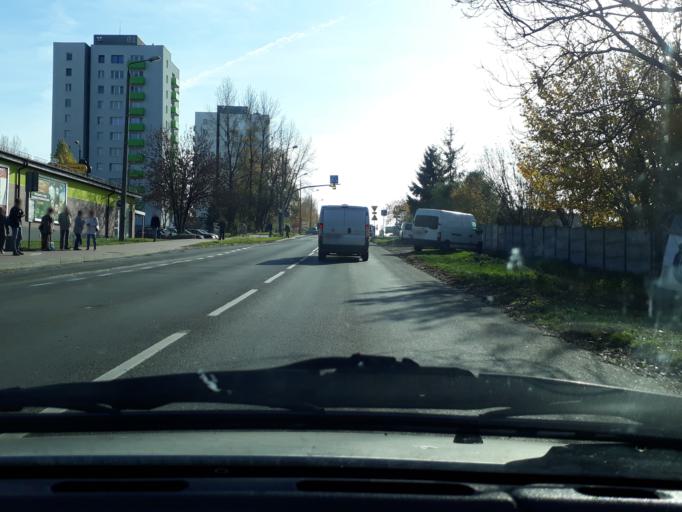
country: PL
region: Silesian Voivodeship
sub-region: Powiat tarnogorski
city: Tarnowskie Gory
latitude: 50.4337
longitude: 18.8647
